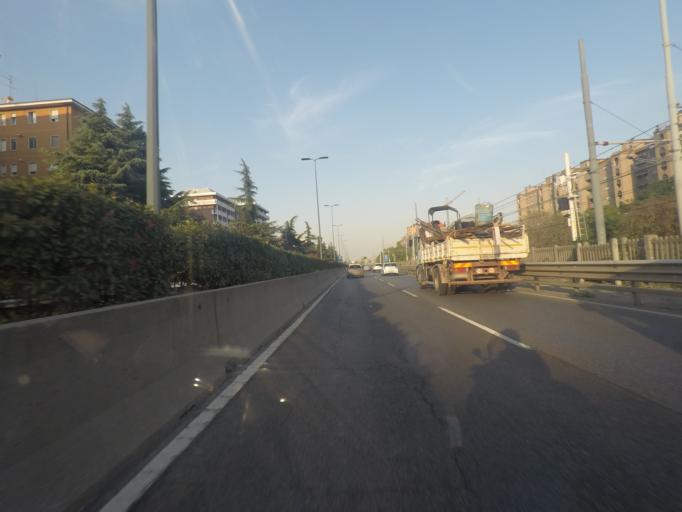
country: IT
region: Lombardy
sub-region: Citta metropolitana di Milano
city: Sesto San Giovanni
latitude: 45.5064
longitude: 9.2496
